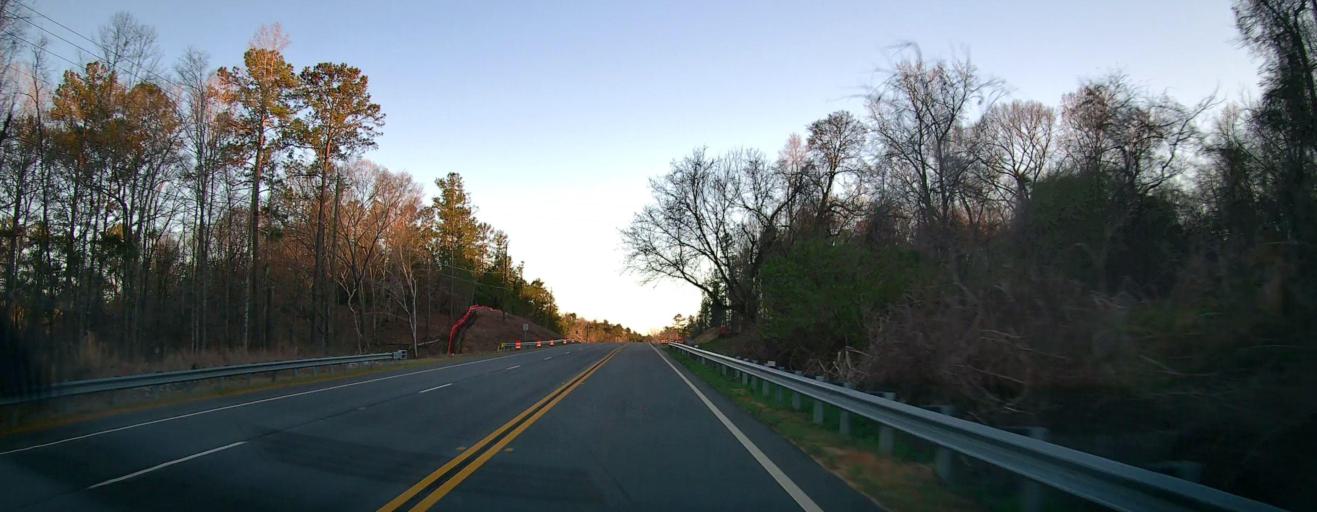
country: US
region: Alabama
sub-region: Lee County
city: Smiths Station
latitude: 32.6058
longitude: -85.0259
